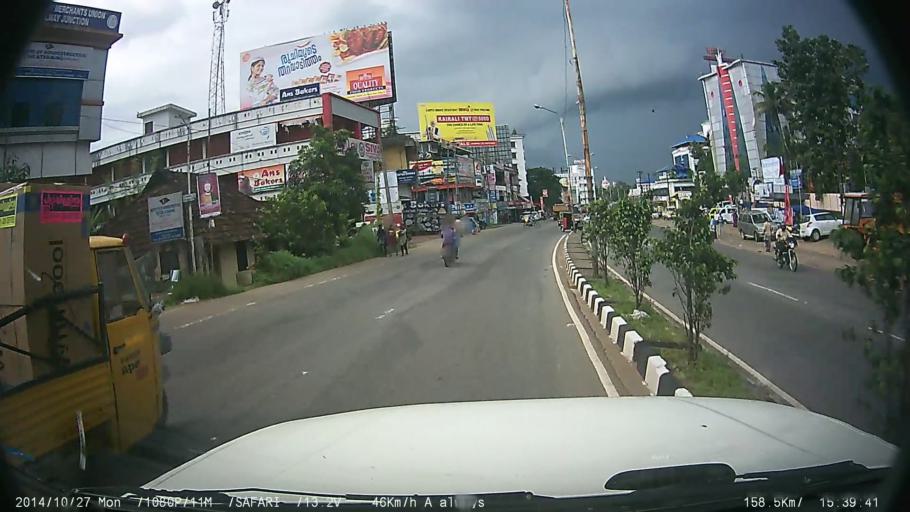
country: IN
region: Kerala
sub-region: Ernakulam
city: Angamali
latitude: 10.1827
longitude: 76.3796
